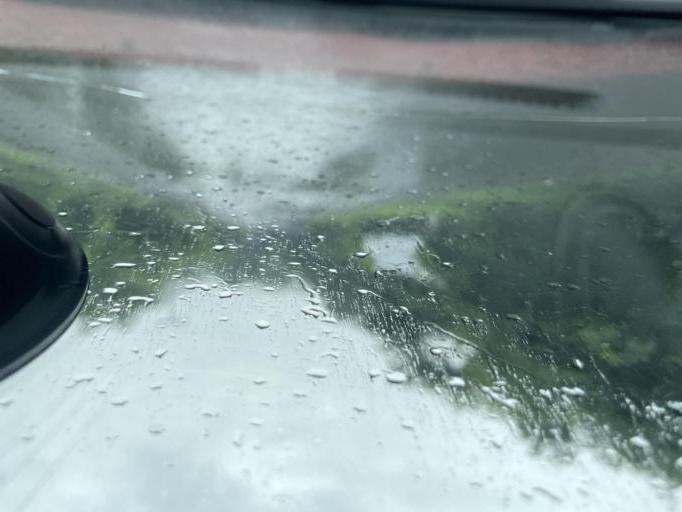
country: SV
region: La Union
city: Santa Rosa de Lima
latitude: 13.6082
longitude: -87.9083
